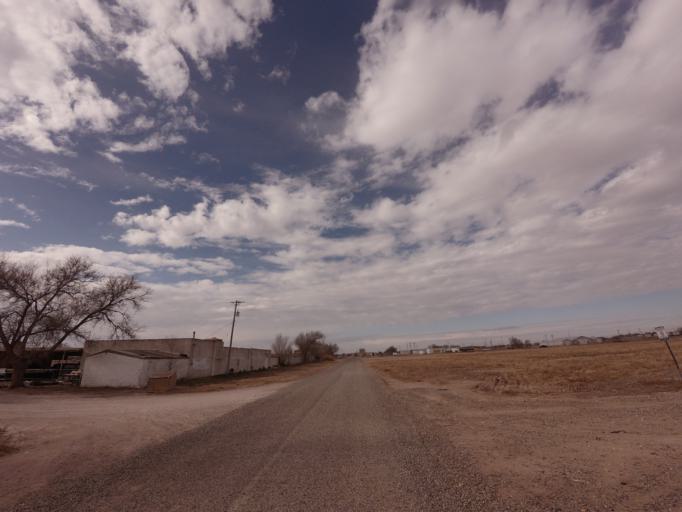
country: US
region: New Mexico
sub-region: Curry County
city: Clovis
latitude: 34.3939
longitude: -103.2179
